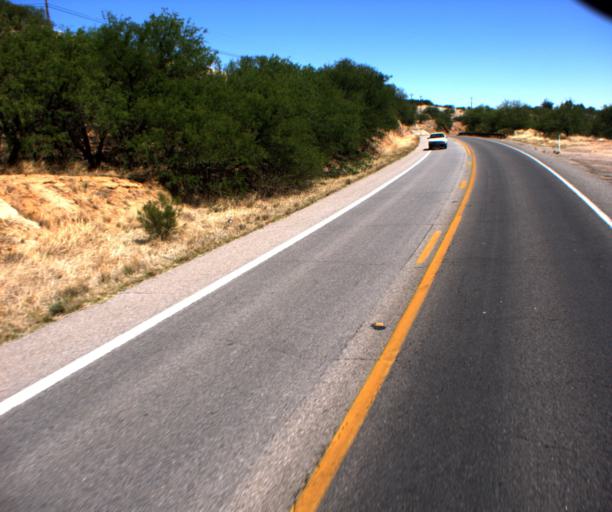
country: US
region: Arizona
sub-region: Santa Cruz County
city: Nogales
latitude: 31.3796
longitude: -110.8848
